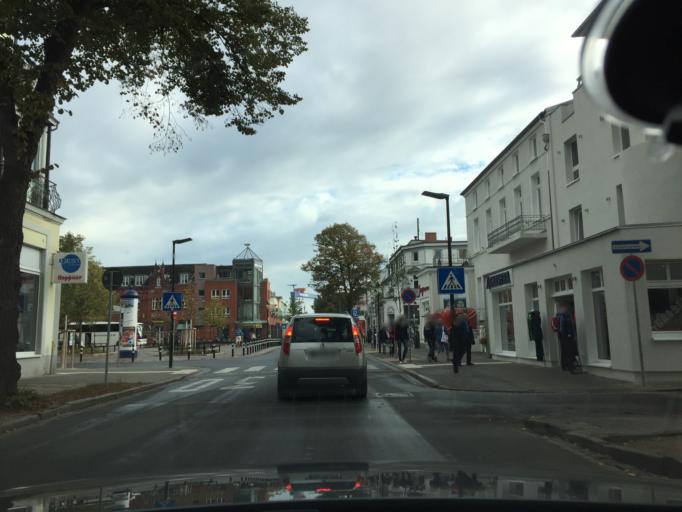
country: DE
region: Mecklenburg-Vorpommern
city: Warnemuende
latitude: 54.1773
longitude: 12.0838
